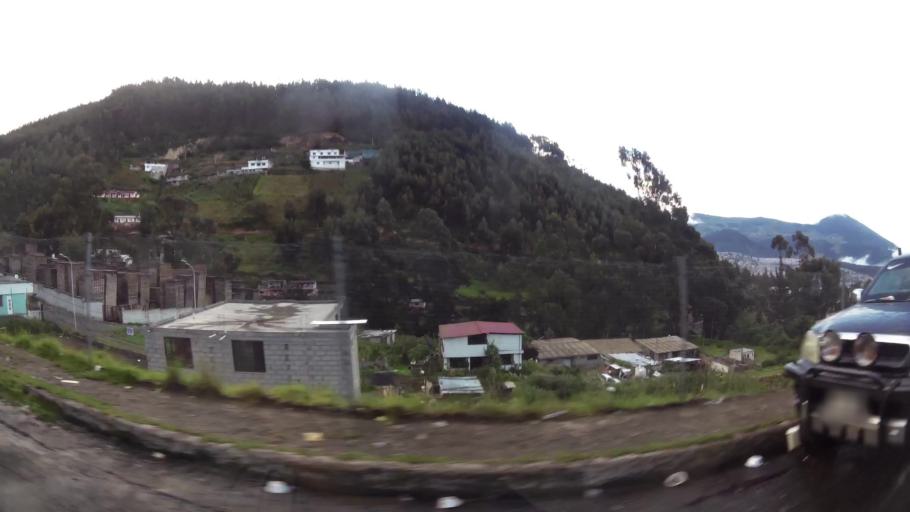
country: EC
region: Pichincha
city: Quito
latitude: -0.1171
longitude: -78.5119
